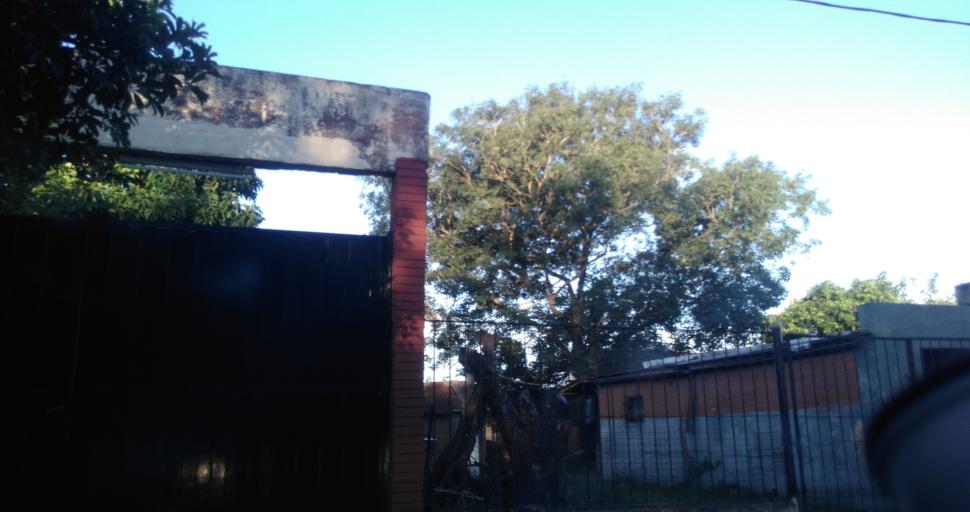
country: AR
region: Chaco
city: Resistencia
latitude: -27.4556
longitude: -58.9692
